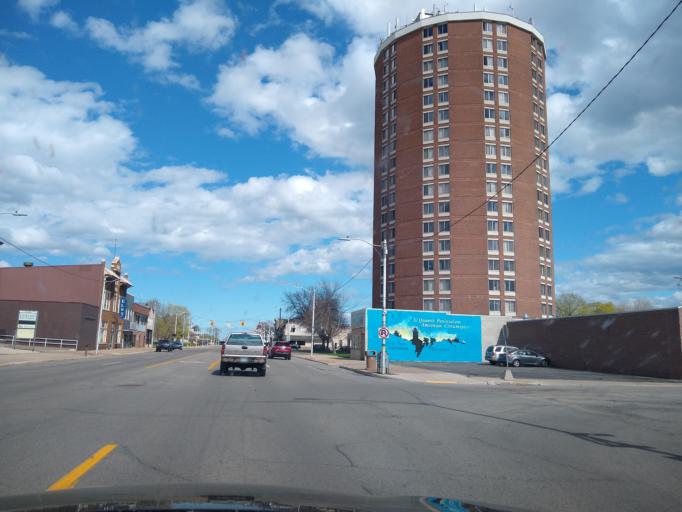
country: US
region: Michigan
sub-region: Delta County
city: Escanaba
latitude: 45.7457
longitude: -87.0555
